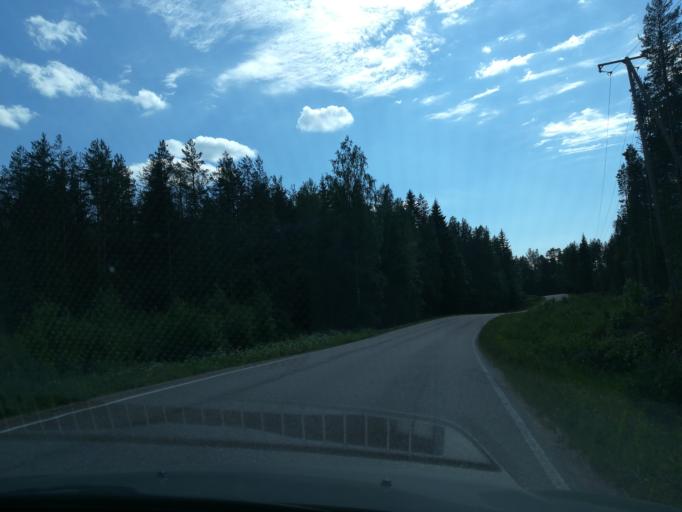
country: FI
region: South Karelia
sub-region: Imatra
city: Ruokolahti
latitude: 61.4869
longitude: 28.7882
